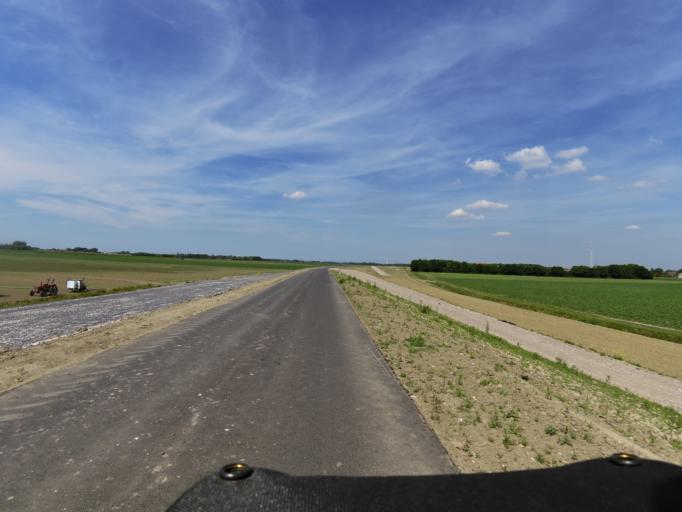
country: NL
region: South Holland
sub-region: Gemeente Spijkenisse
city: Spijkenisse
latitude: 51.7913
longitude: 4.2647
